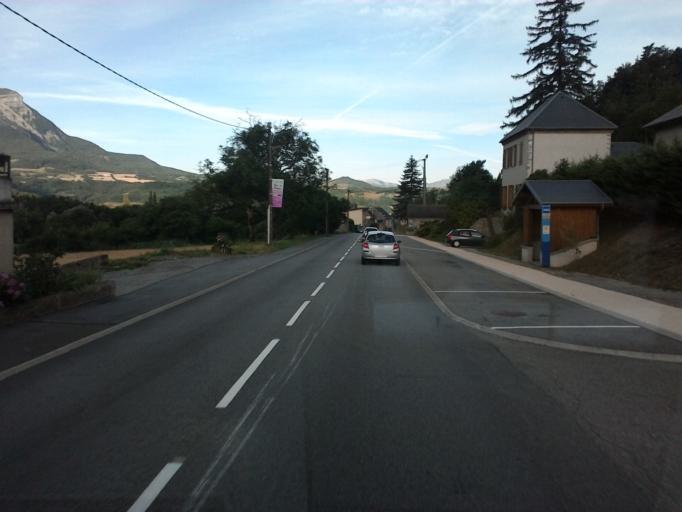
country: FR
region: Rhone-Alpes
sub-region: Departement de l'Isere
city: La Mure
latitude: 44.8641
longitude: 5.8609
